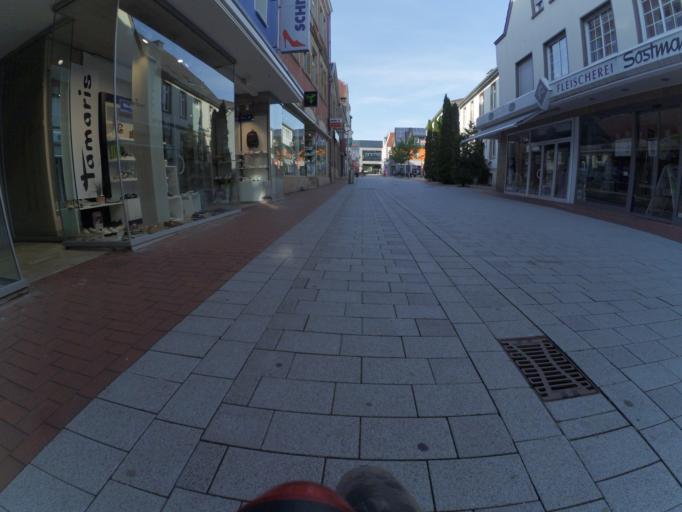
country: DE
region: North Rhine-Westphalia
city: Ibbenburen
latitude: 52.2772
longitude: 7.7158
